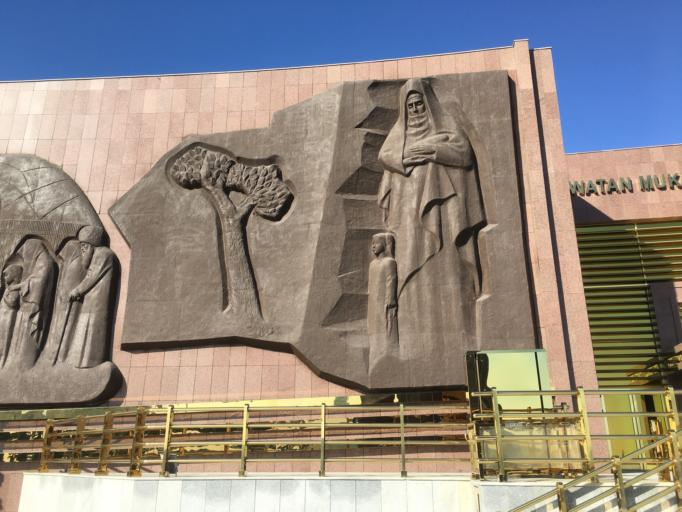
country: TM
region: Ahal
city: Ashgabat
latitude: 37.9372
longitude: 58.3125
